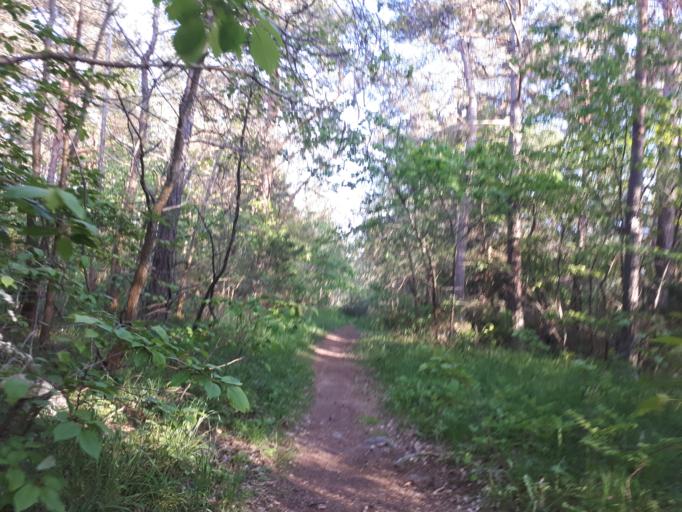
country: SE
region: Gotland
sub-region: Gotland
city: Visby
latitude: 57.6079
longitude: 18.2958
